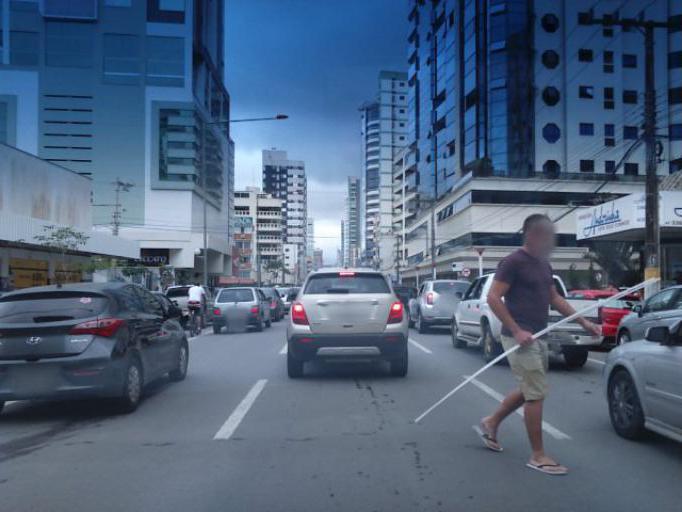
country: BR
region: Santa Catarina
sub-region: Itapema
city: Itapema
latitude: -27.1219
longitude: -48.6061
